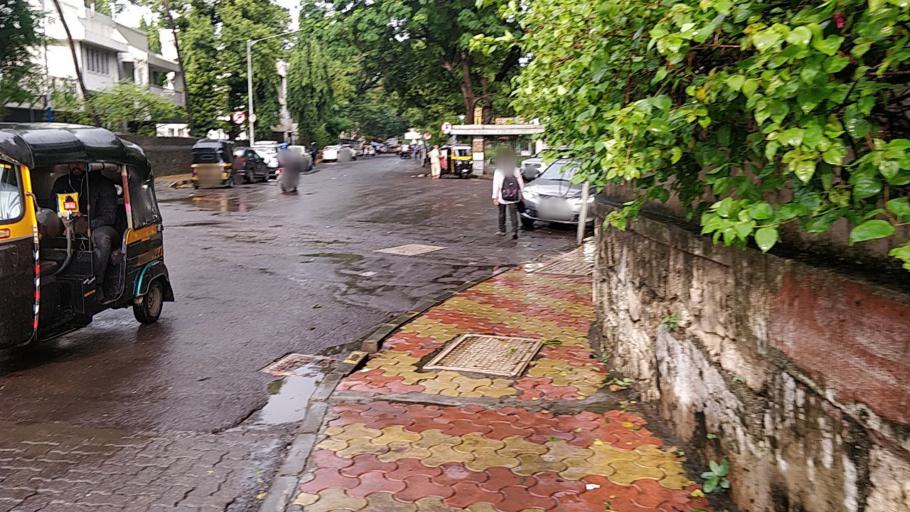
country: IN
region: Maharashtra
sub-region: Mumbai Suburban
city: Mumbai
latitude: 19.0982
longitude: 72.8397
